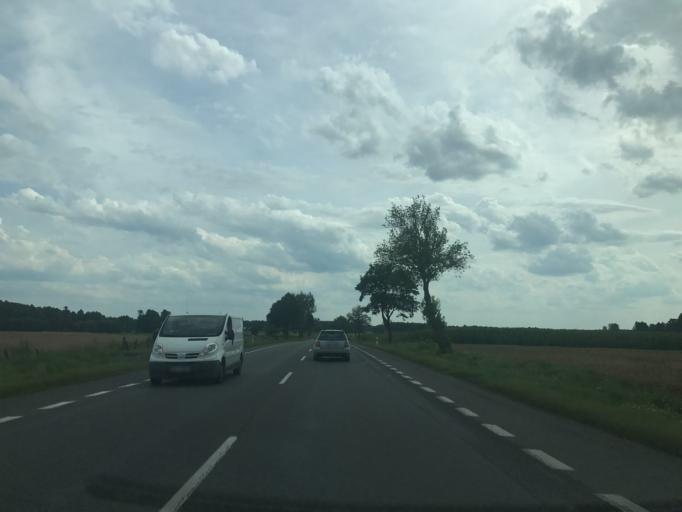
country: PL
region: Masovian Voivodeship
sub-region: Powiat mlawski
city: Strzegowo
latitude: 52.9388
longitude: 20.2830
